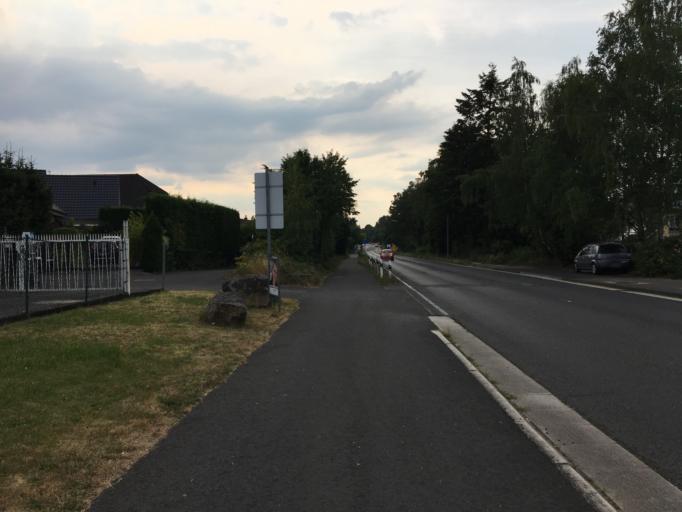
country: DE
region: North Rhine-Westphalia
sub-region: Regierungsbezirk Koln
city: Rosrath
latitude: 50.8980
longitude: 7.1678
